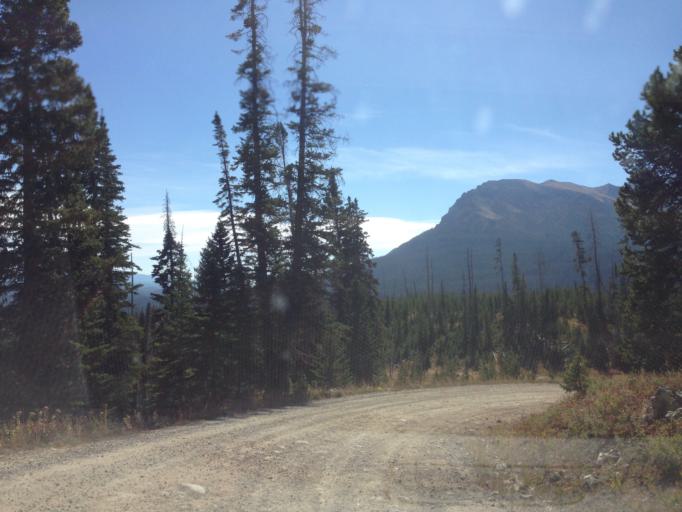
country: US
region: Montana
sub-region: Stillwater County
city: Absarokee
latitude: 45.0350
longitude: -109.9117
